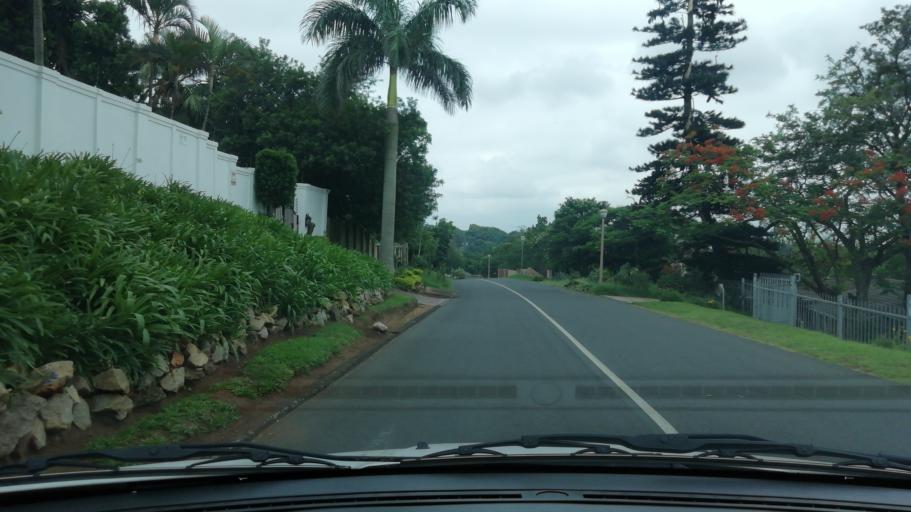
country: ZA
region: KwaZulu-Natal
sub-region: uThungulu District Municipality
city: Empangeni
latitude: -28.7598
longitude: 31.8888
